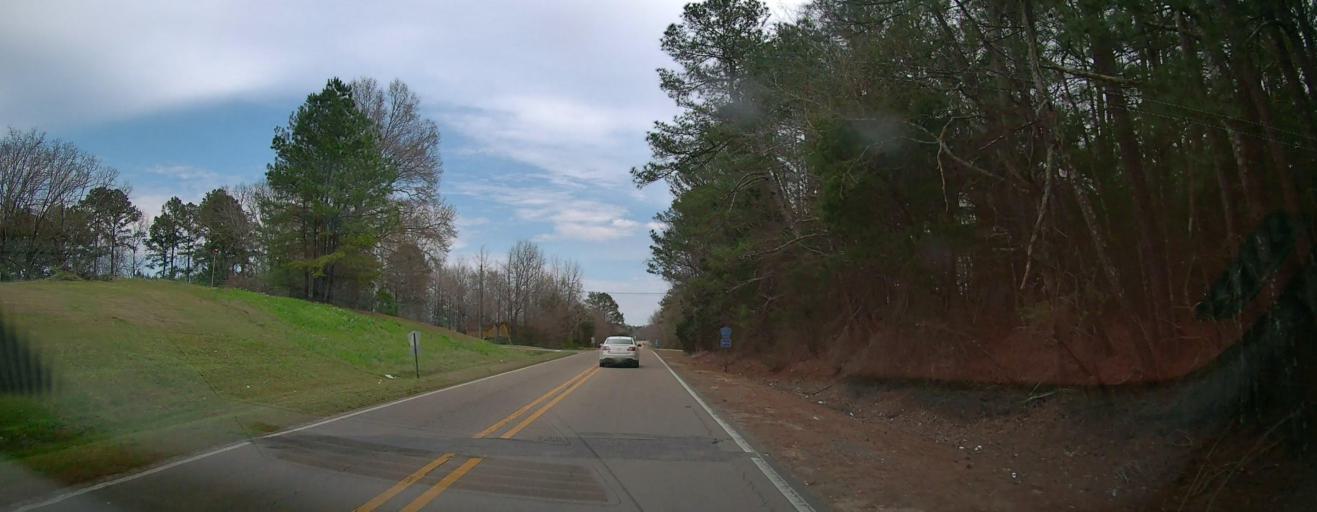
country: US
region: Mississippi
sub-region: Itawamba County
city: Mantachie
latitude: 34.2668
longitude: -88.5706
